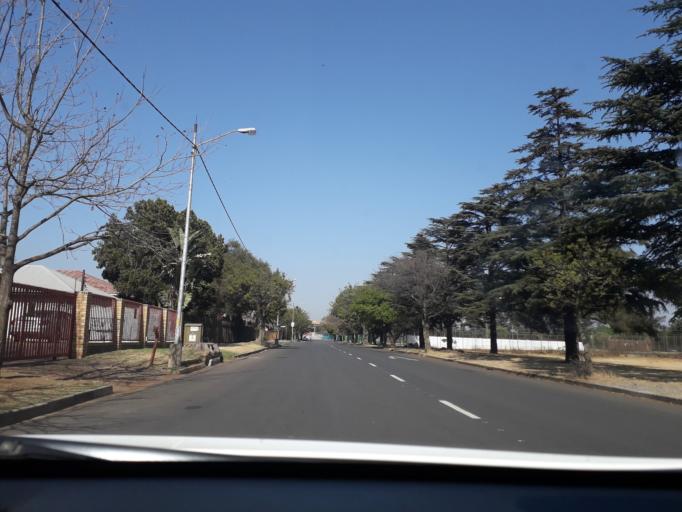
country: ZA
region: Gauteng
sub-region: City of Johannesburg Metropolitan Municipality
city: Modderfontein
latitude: -26.1004
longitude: 28.2410
